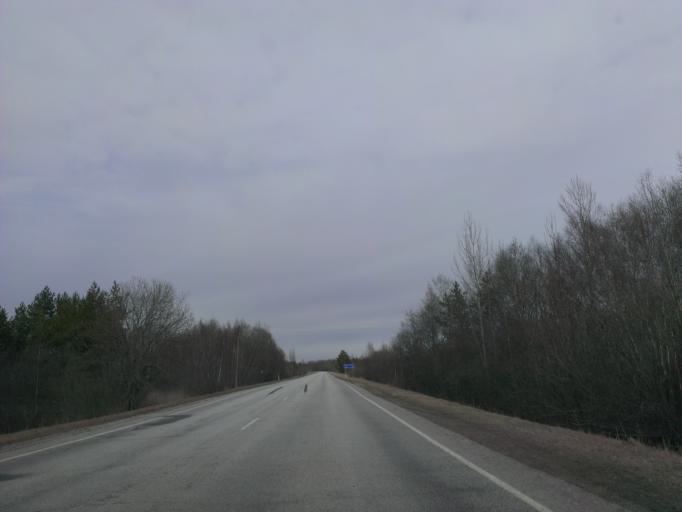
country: EE
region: Laeaene
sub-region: Lihula vald
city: Lihula
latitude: 58.5933
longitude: 23.5426
